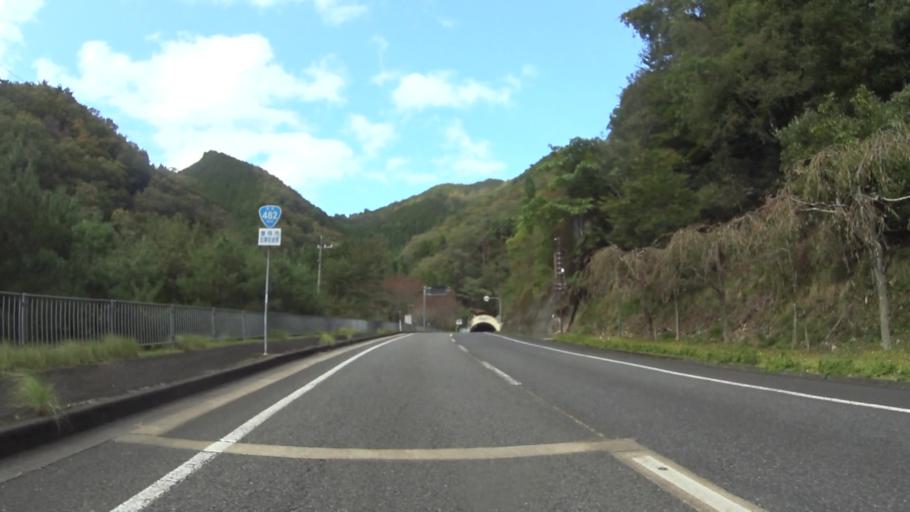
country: JP
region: Hyogo
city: Toyooka
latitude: 35.5223
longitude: 134.9879
